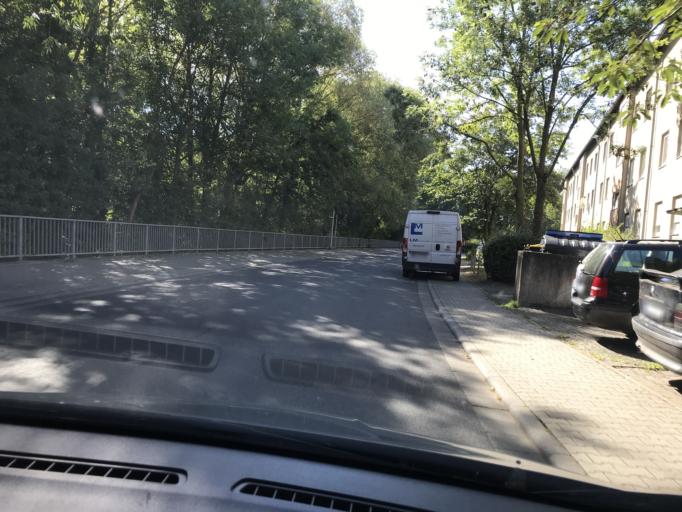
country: DE
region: Hesse
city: Gross-Umstadt
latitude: 49.8764
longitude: 8.9269
